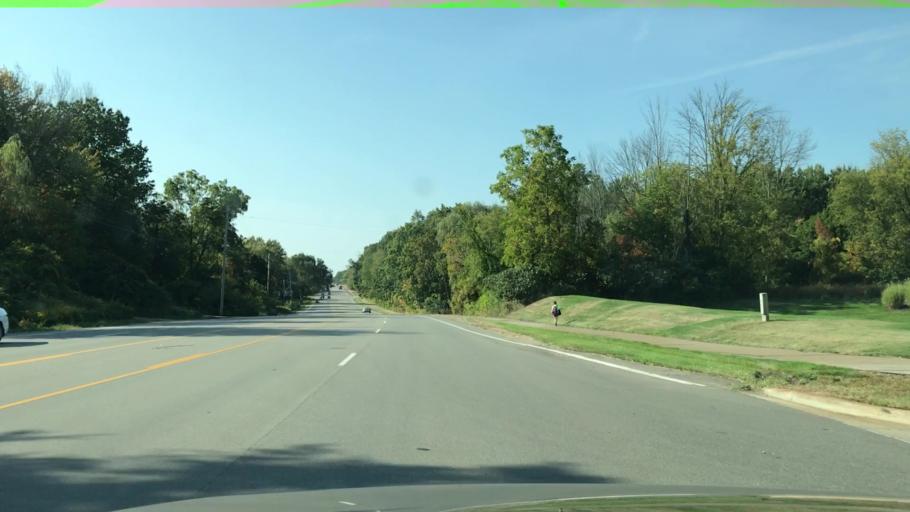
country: US
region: Michigan
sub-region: Kent County
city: Forest Hills
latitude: 42.9323
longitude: -85.5235
